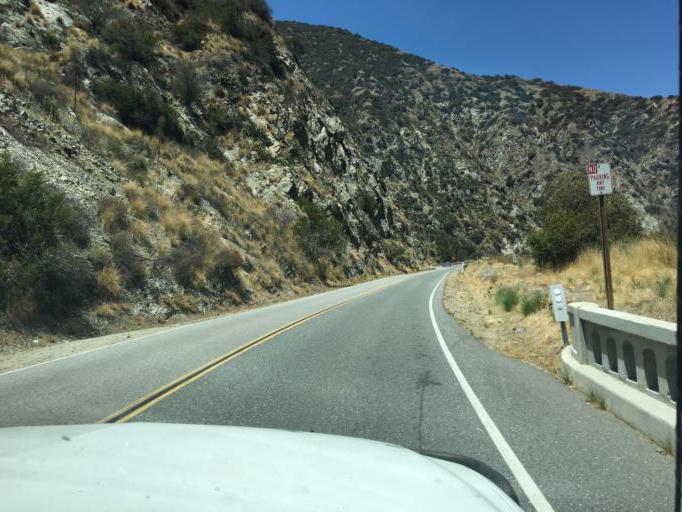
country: US
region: California
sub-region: Los Angeles County
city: Azusa
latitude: 34.1674
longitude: -117.8923
